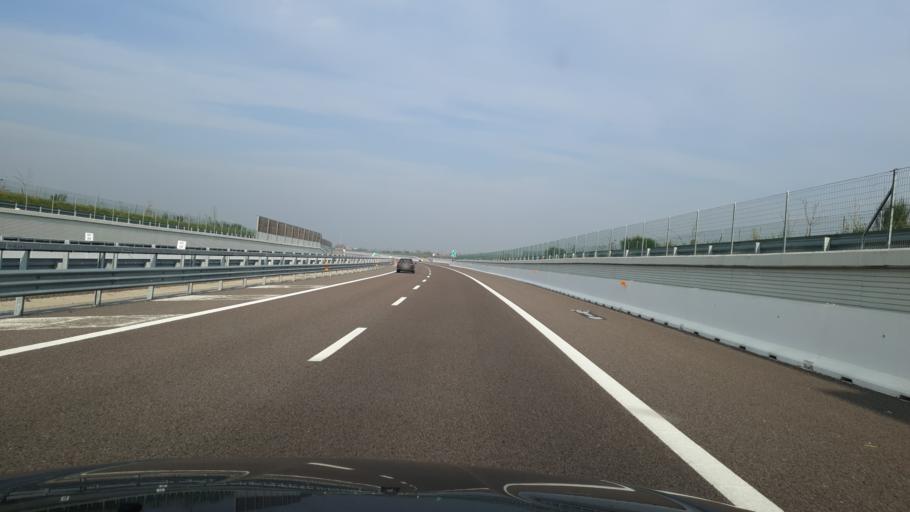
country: IT
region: Veneto
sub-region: Provincia di Vicenza
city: Agugliaro
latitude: 45.3076
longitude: 11.5792
